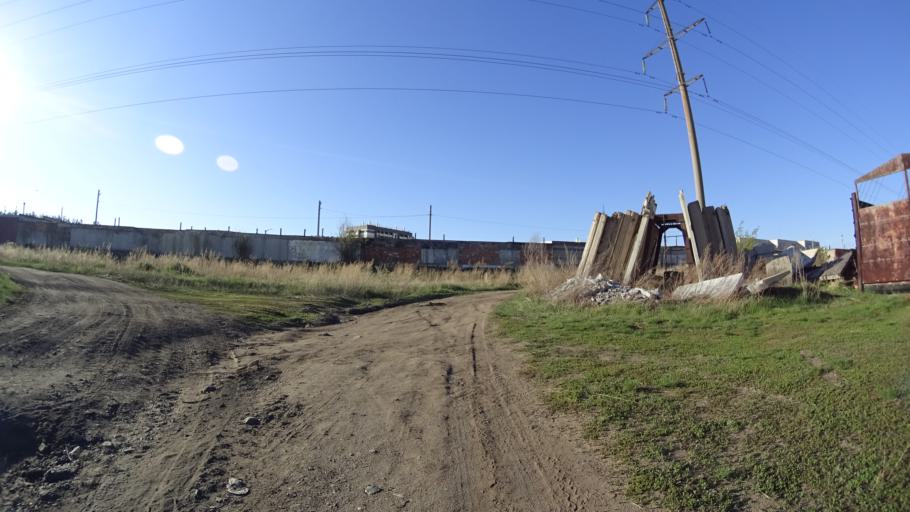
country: RU
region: Chelyabinsk
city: Troitsk
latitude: 54.0702
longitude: 61.5314
